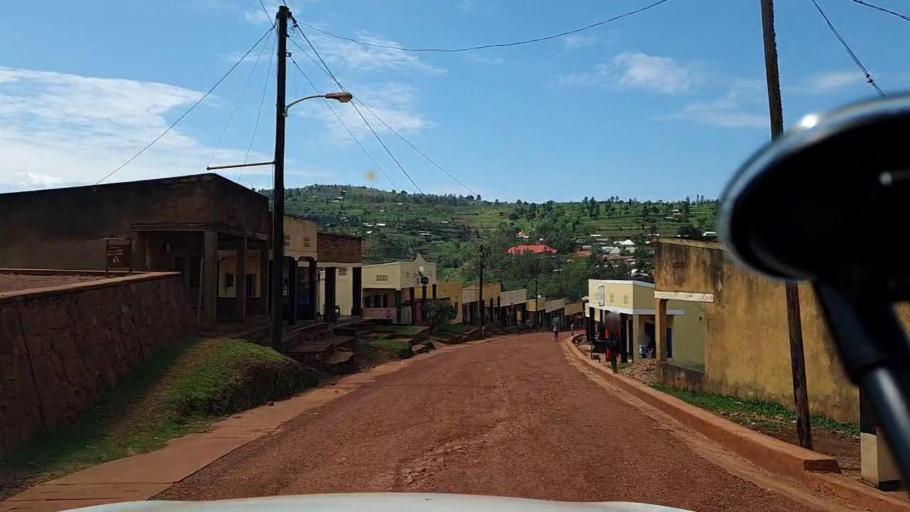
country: RW
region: Kigali
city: Kigali
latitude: -1.8024
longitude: 29.8941
